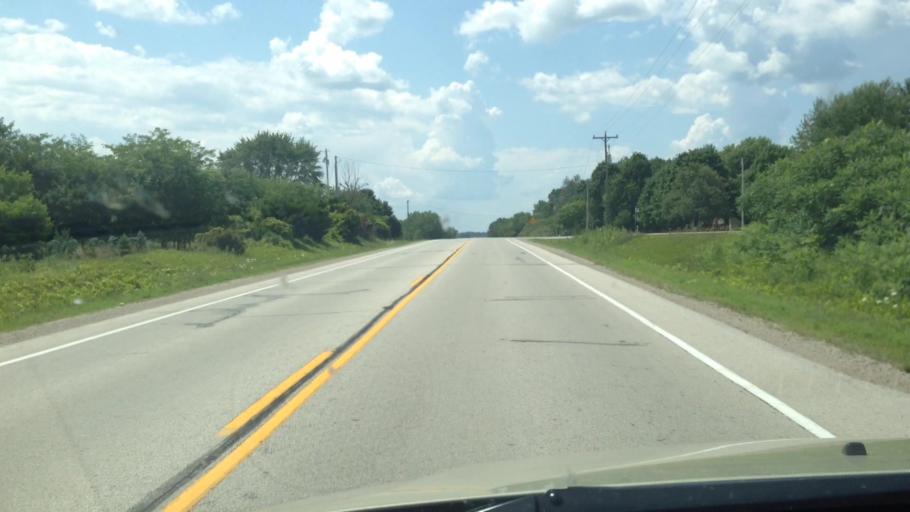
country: US
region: Wisconsin
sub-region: Brown County
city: Suamico
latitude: 44.6477
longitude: -88.1368
